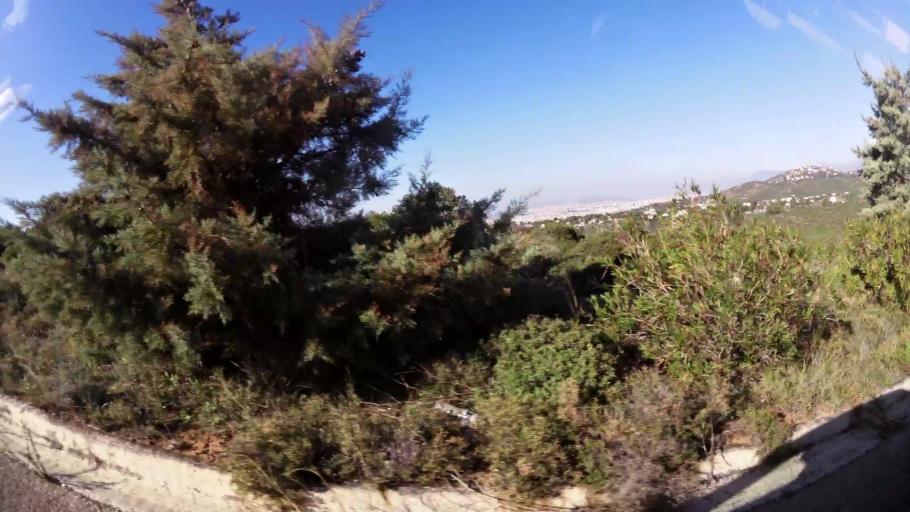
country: GR
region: Attica
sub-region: Nomarchia Anatolikis Attikis
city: Anthousa
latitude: 38.0312
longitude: 23.8923
